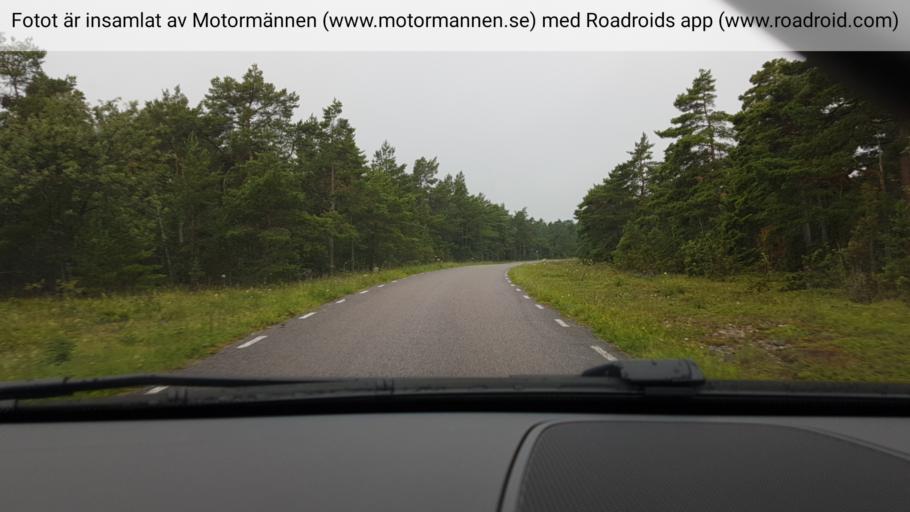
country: SE
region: Gotland
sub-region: Gotland
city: Slite
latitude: 57.8914
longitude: 18.7425
